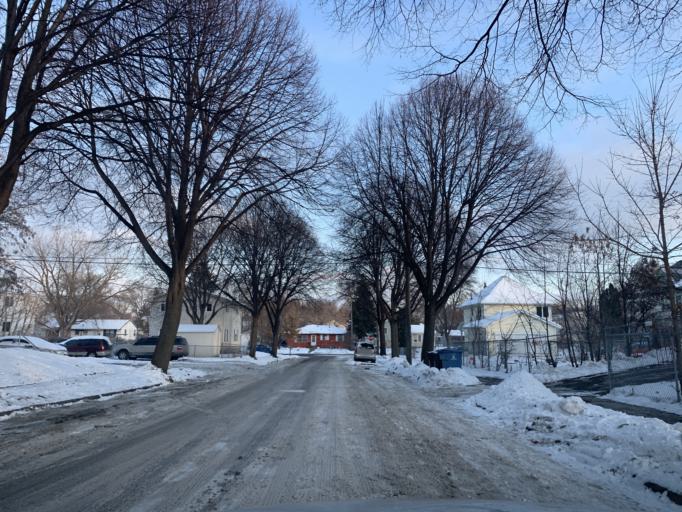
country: US
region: Minnesota
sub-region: Hennepin County
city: Minneapolis
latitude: 44.9897
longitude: -93.3031
